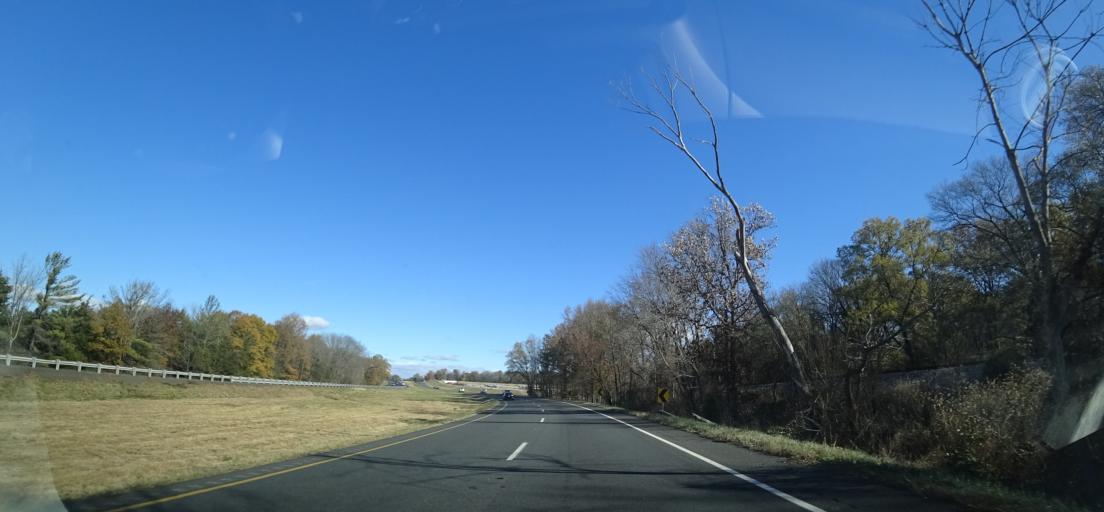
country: US
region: Virginia
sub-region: Fauquier County
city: Bealeton
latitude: 38.5172
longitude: -77.8386
